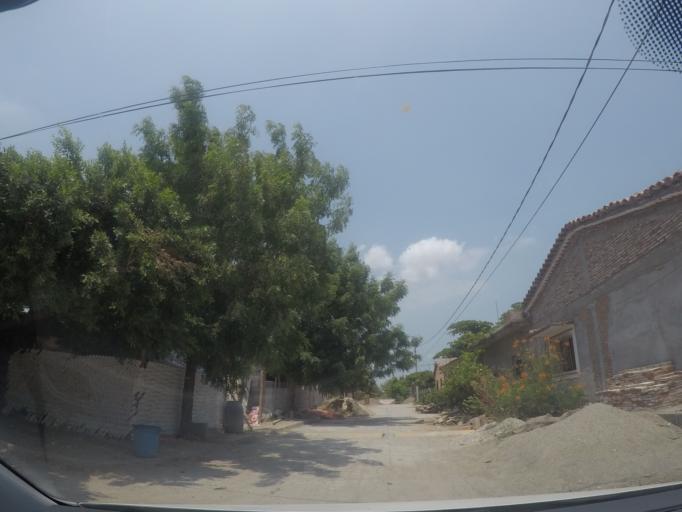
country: MX
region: Oaxaca
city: Asuncion Ixtaltepec
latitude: 16.5062
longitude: -95.0563
